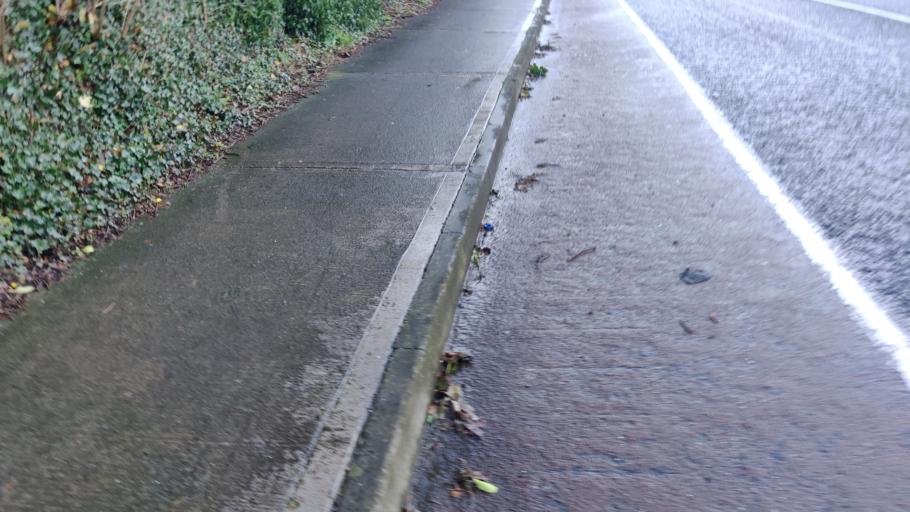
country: IE
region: Munster
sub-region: County Cork
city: Cork
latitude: 51.8713
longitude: -8.4193
